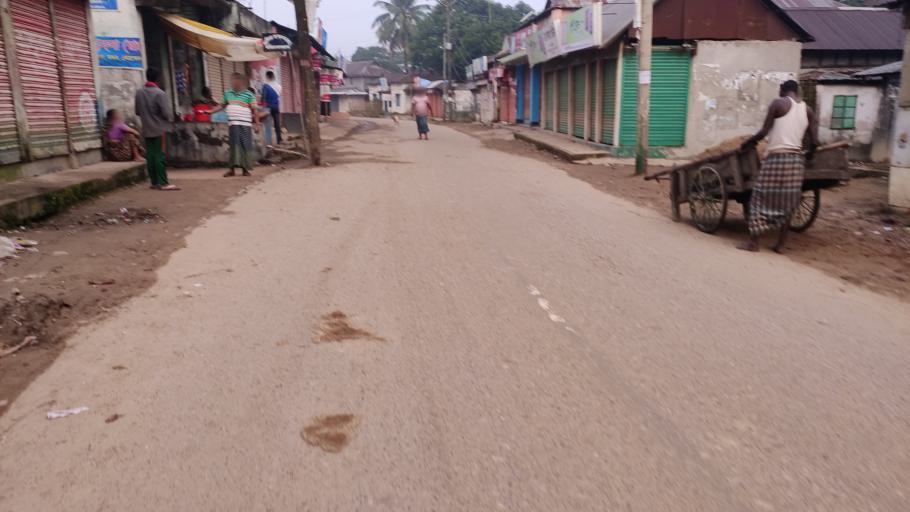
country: BD
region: Dhaka
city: Netrakona
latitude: 24.7167
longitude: 90.9539
